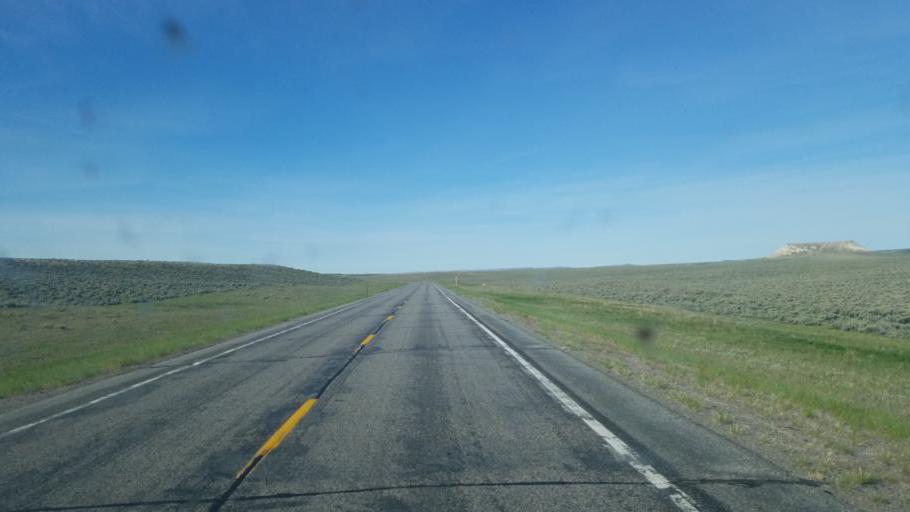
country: US
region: Wyoming
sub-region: Fremont County
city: Riverton
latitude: 42.6525
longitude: -108.1903
